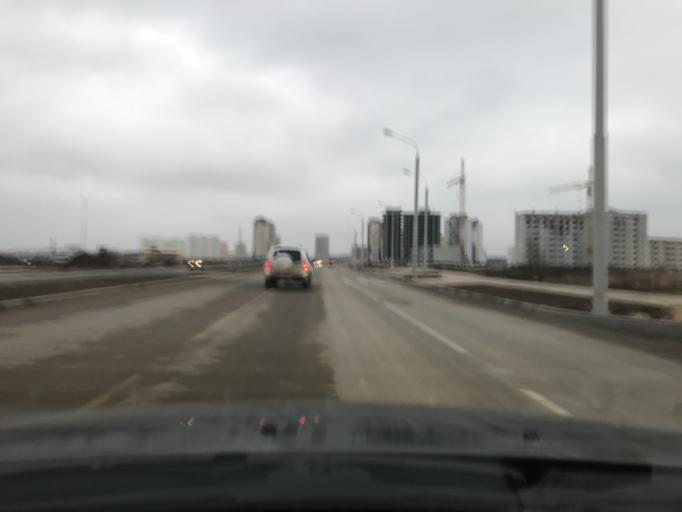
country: RU
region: Kaluga
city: Mstikhino
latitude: 54.4915
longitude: 36.1810
